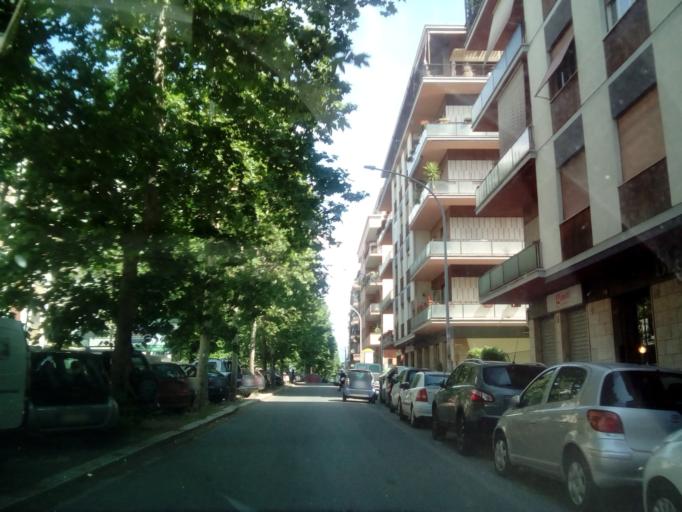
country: IT
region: Latium
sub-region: Citta metropolitana di Roma Capitale
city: Rome
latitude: 41.8542
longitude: 12.5614
